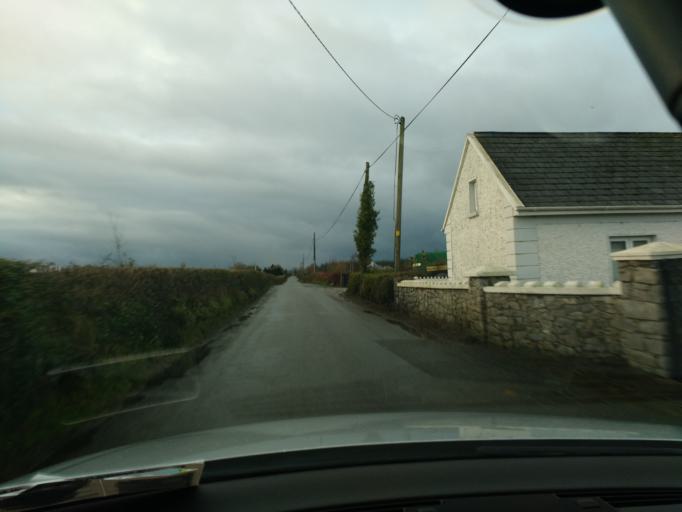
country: IE
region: Munster
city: Thurles
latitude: 52.6359
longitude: -7.8386
